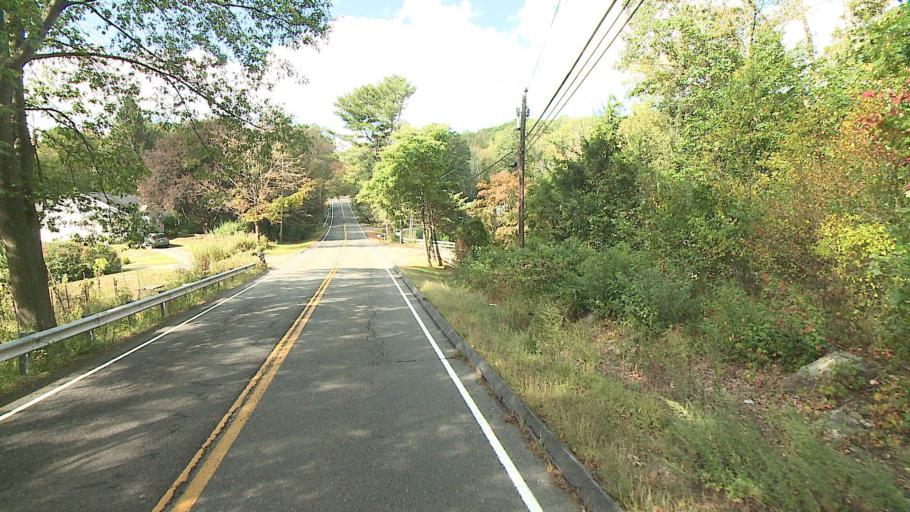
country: US
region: Connecticut
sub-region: New Haven County
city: Prospect
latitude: 41.4533
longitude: -73.0038
